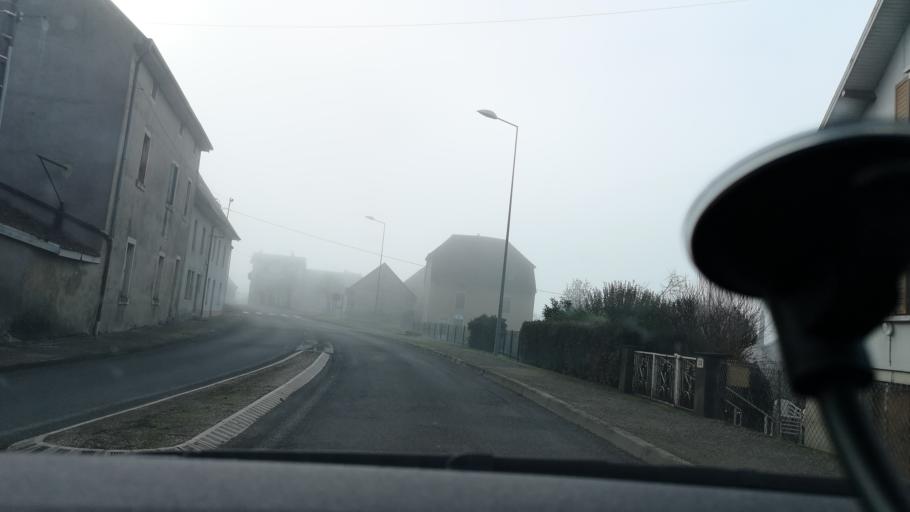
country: FR
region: Franche-Comte
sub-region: Departement du Doubs
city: Clerval
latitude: 47.4267
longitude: 6.5622
